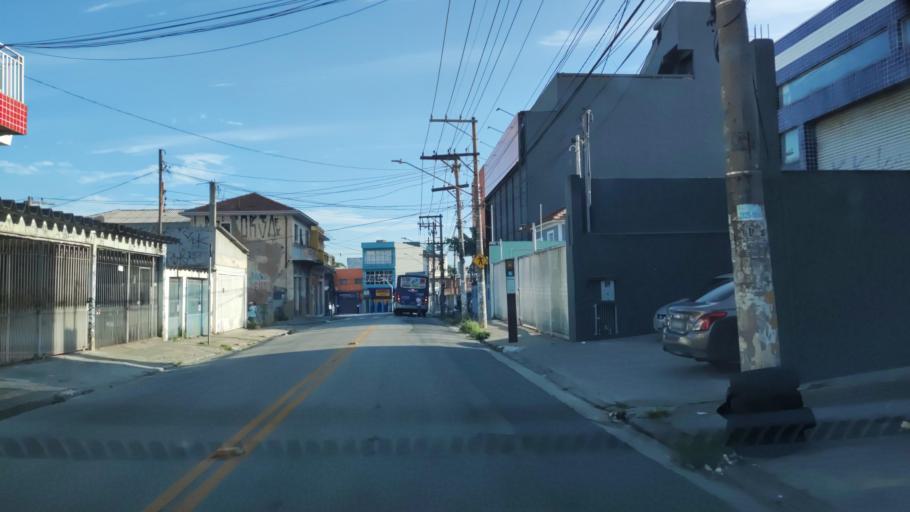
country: BR
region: Sao Paulo
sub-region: Osasco
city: Osasco
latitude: -23.5161
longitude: -46.7537
